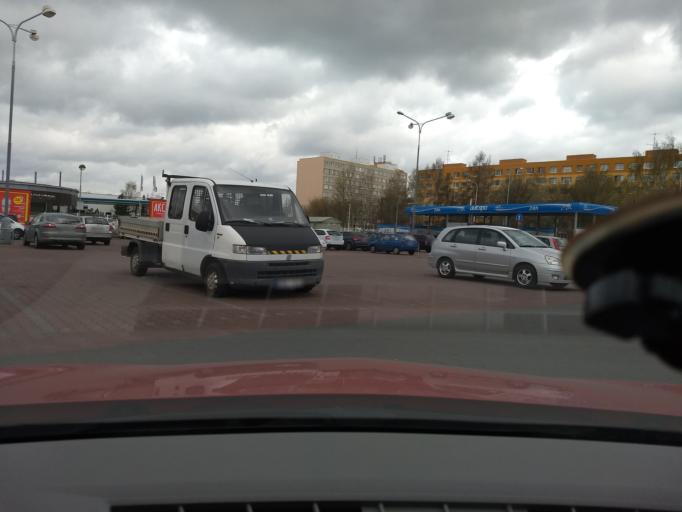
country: CZ
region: Central Bohemia
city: Kladno
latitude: 50.1265
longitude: 14.1229
